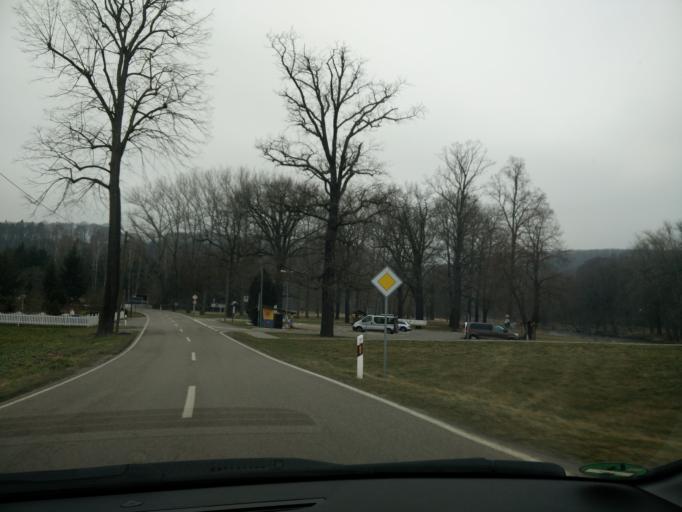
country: DE
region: Saxony
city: Wechselburg
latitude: 51.0030
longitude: 12.7678
